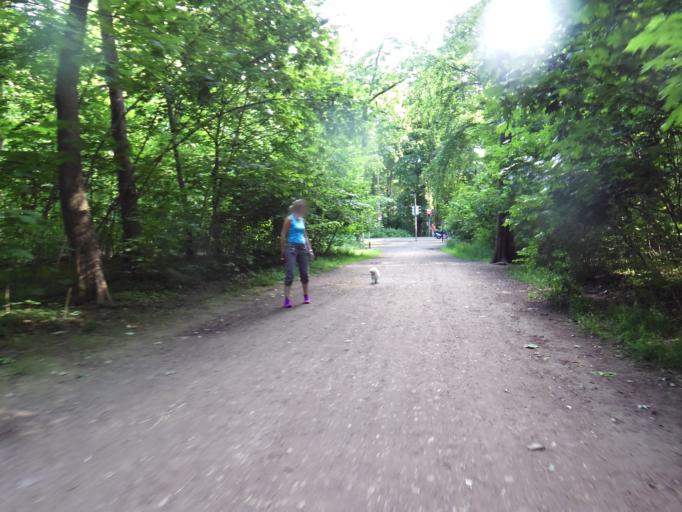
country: DE
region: Saxony
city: Leipzig
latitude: 51.3478
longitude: 12.3607
